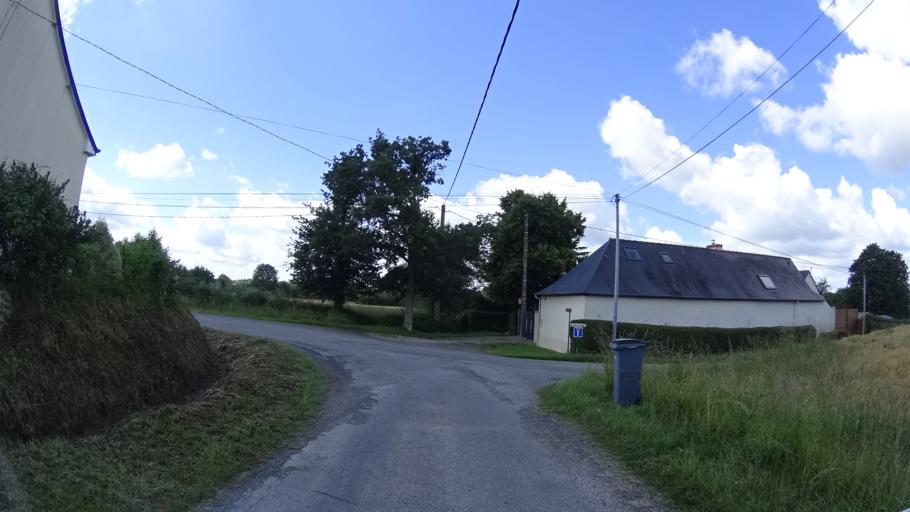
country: FR
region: Brittany
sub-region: Departement d'Ille-et-Vilaine
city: Le Rheu
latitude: 48.1119
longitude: -1.8075
